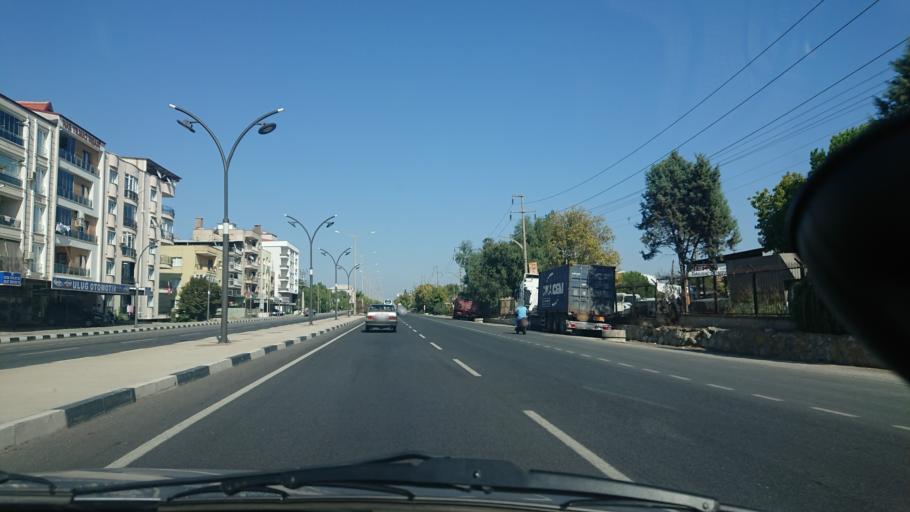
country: TR
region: Manisa
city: Turgutlu
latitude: 38.4925
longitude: 27.7121
